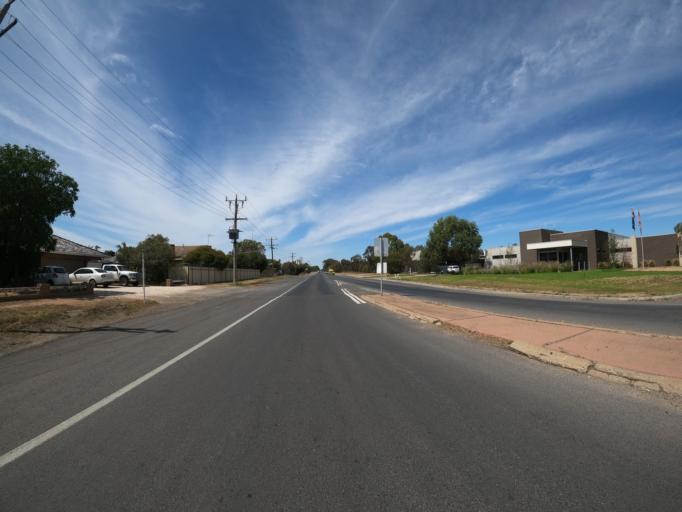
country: AU
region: Victoria
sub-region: Moira
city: Yarrawonga
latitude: -36.0207
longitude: 145.9956
